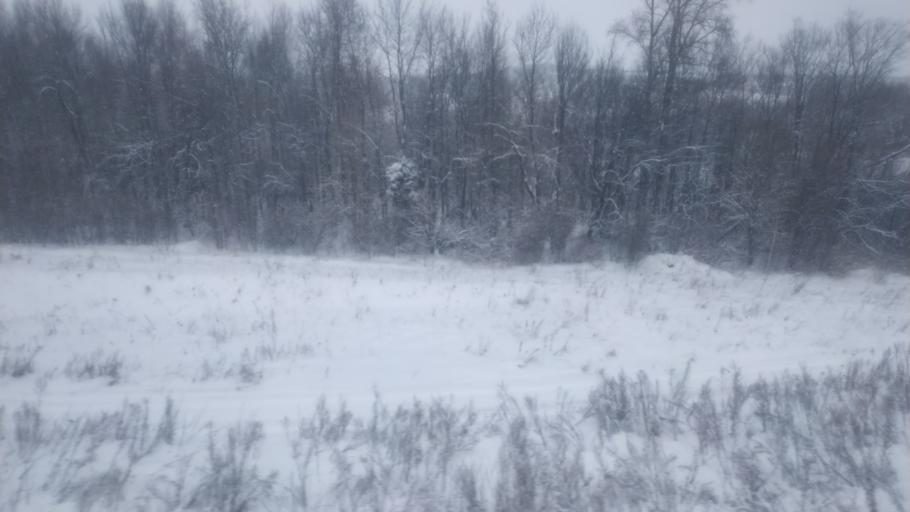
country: RU
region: Udmurtiya
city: Kiyasovo
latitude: 56.5019
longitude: 53.3648
